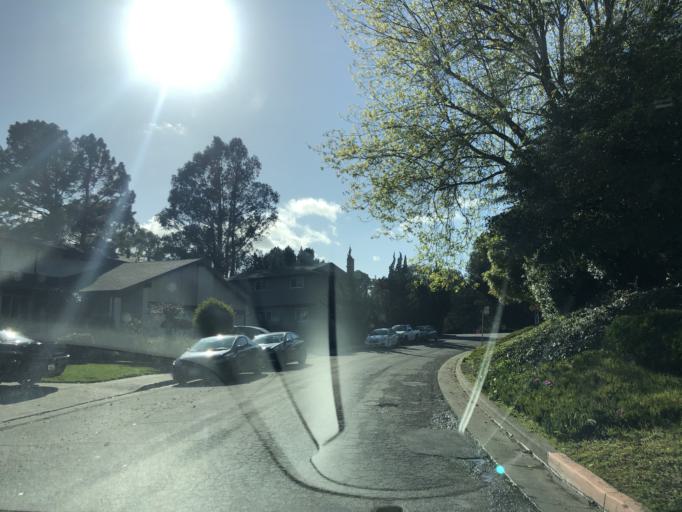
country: US
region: California
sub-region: Contra Costa County
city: El Sobrante
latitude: 37.9807
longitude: -122.3086
